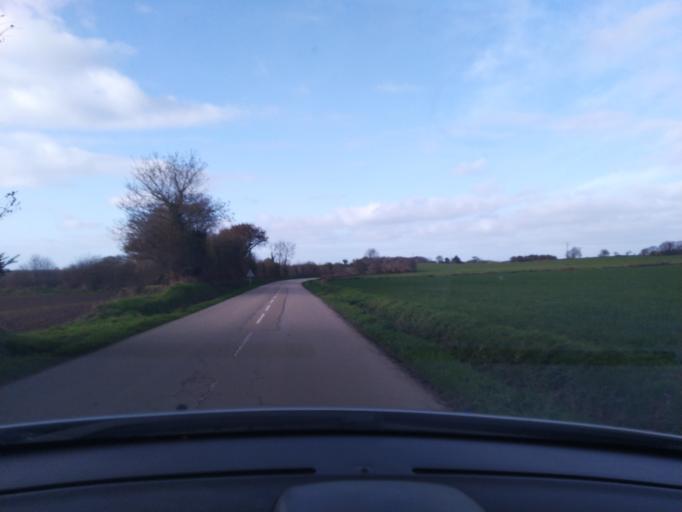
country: FR
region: Brittany
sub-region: Departement du Finistere
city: Plouigneau
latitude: 48.5348
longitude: -3.6713
